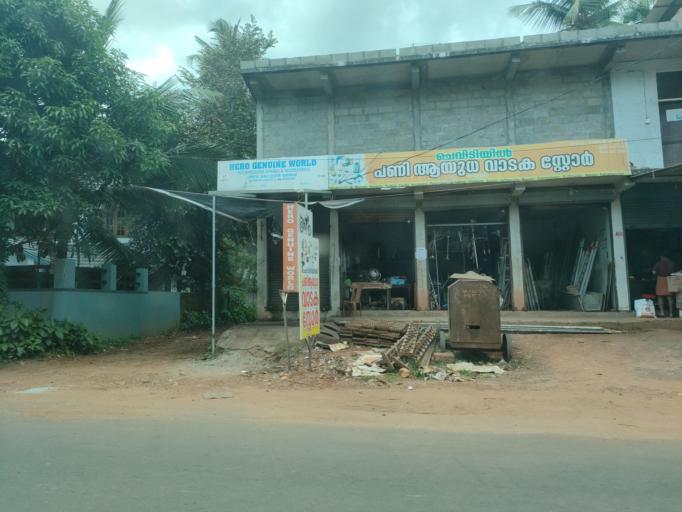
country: IN
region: Kerala
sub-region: Kozhikode
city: Mavoor
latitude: 11.2631
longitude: 75.8976
